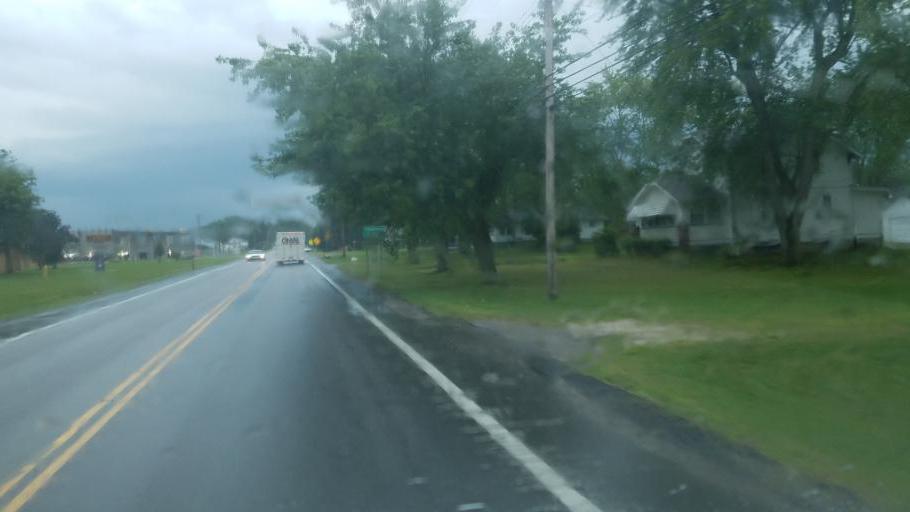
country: US
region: Ohio
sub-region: Trumbull County
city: Champion Heights
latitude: 41.3167
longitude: -80.8530
